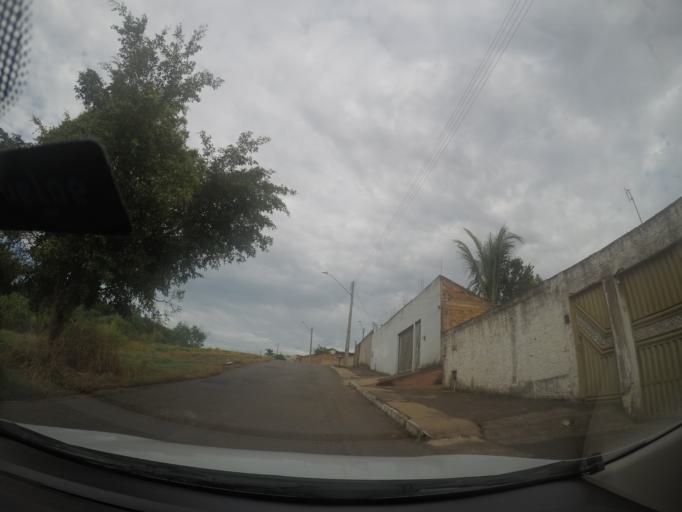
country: BR
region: Goias
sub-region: Goiania
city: Goiania
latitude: -16.6755
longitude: -49.2037
